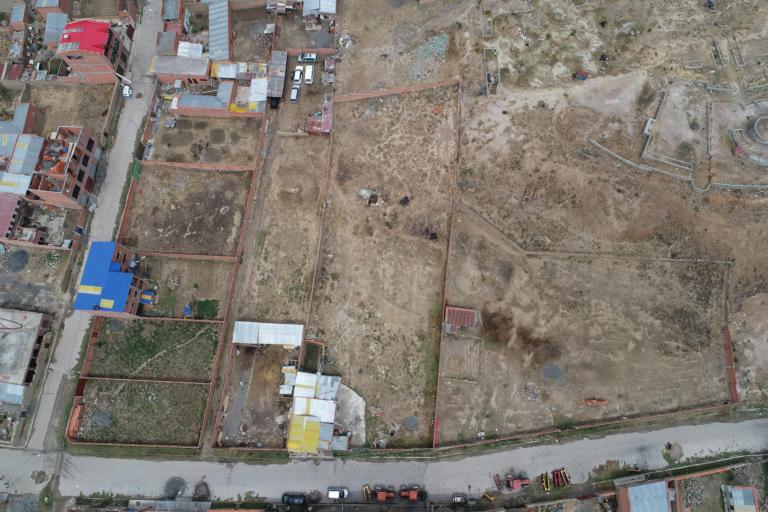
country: BO
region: La Paz
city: Achacachi
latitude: -16.0510
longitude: -68.6832
